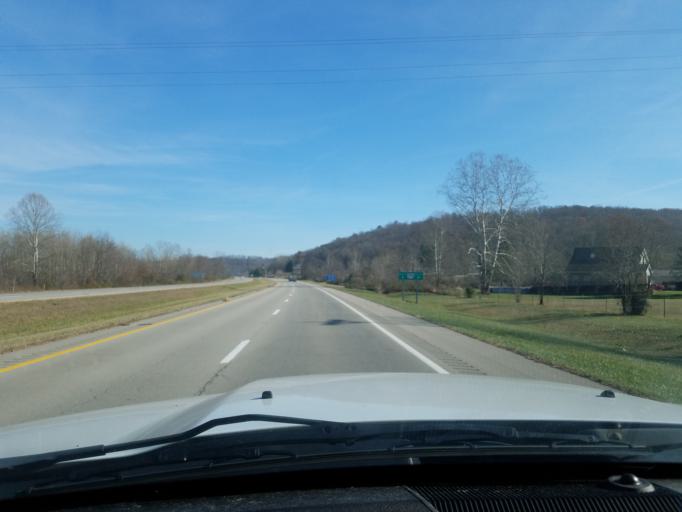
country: US
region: Ohio
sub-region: Pike County
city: Piketon
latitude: 39.0432
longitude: -83.1513
